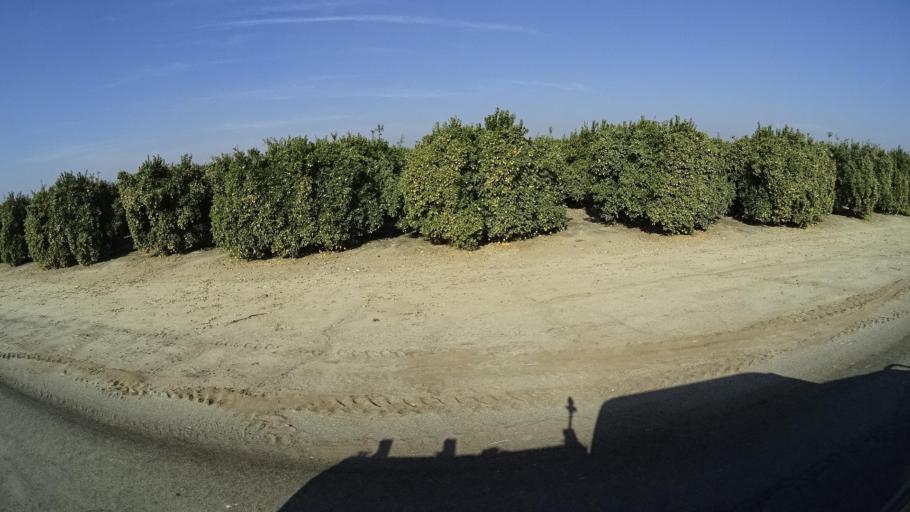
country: US
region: California
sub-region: Kern County
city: McFarland
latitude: 35.6166
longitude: -119.1798
